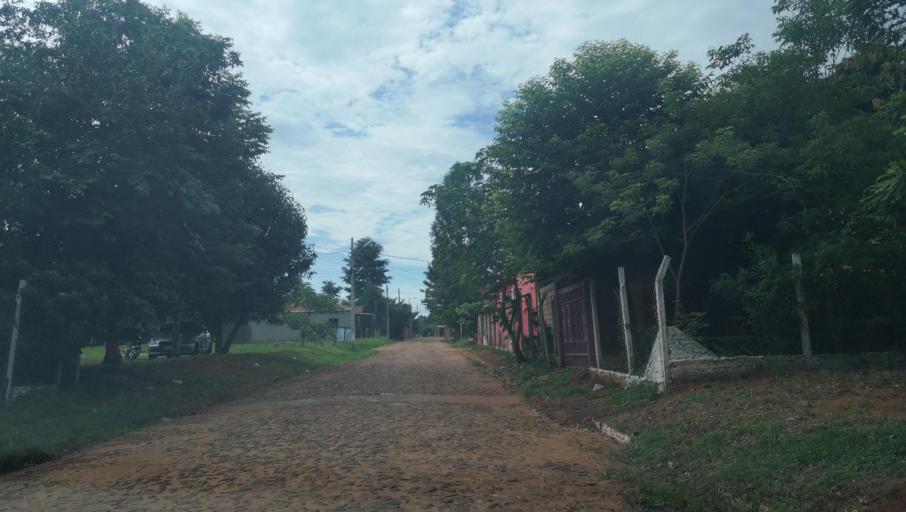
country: PY
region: San Pedro
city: Capiibary
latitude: -24.7213
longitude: -56.0178
